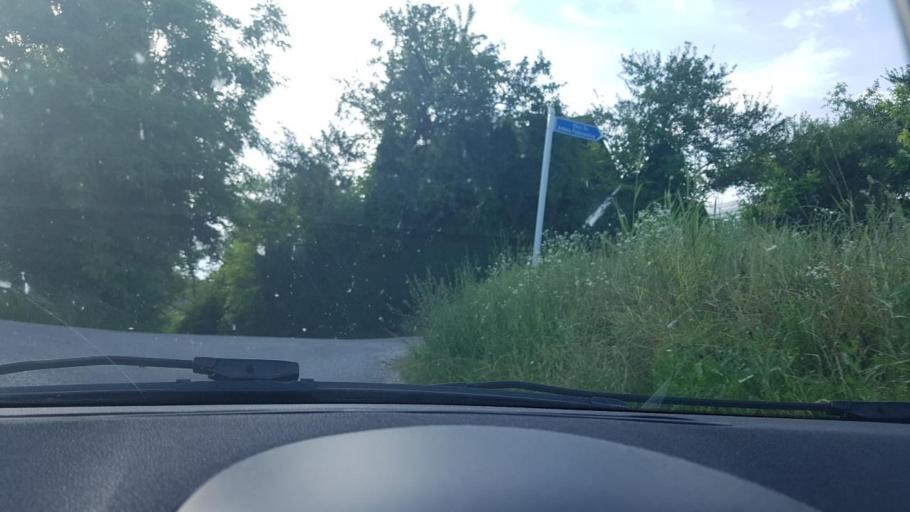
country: HR
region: Krapinsko-Zagorska
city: Zabok
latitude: 46.0373
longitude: 15.9135
